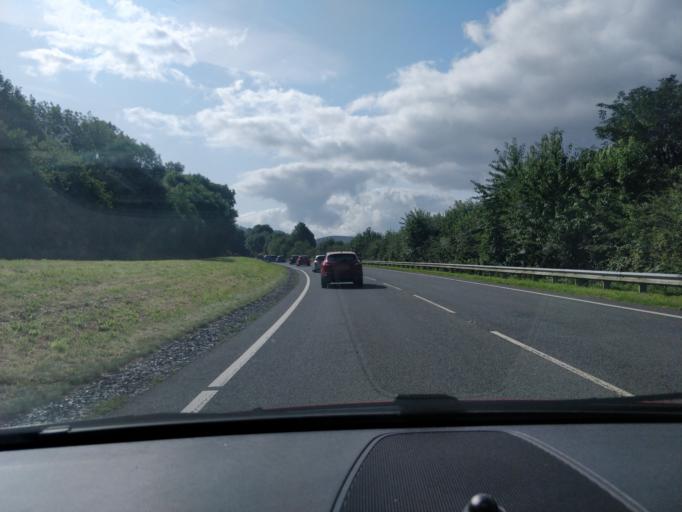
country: GB
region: Wales
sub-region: Conwy
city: Llanrwst
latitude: 53.1489
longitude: -3.8056
